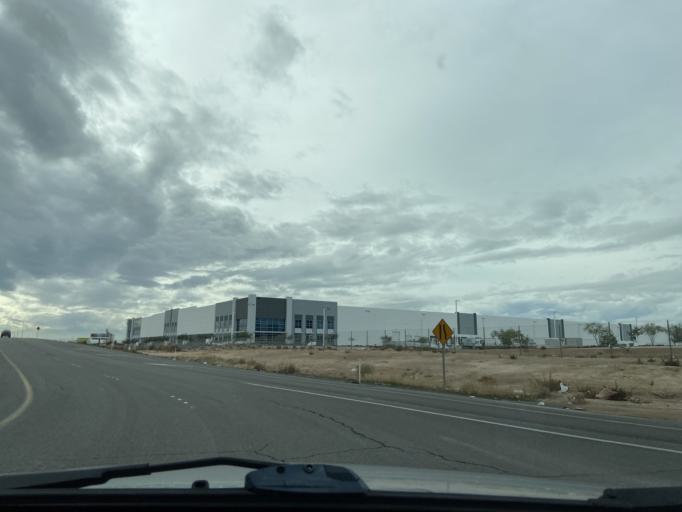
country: US
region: Nevada
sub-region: Clark County
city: Nellis Air Force Base
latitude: 36.2584
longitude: -115.0804
